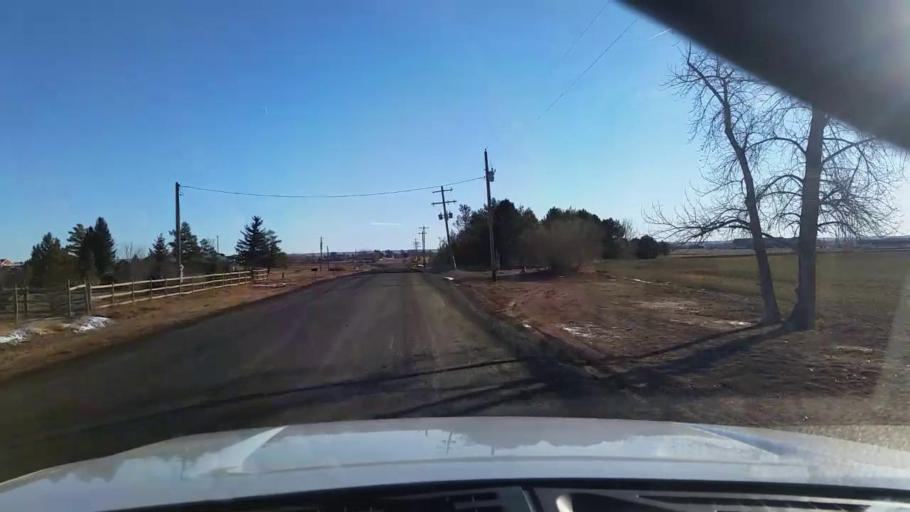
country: US
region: Colorado
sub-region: Larimer County
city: Wellington
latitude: 40.7696
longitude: -105.0800
